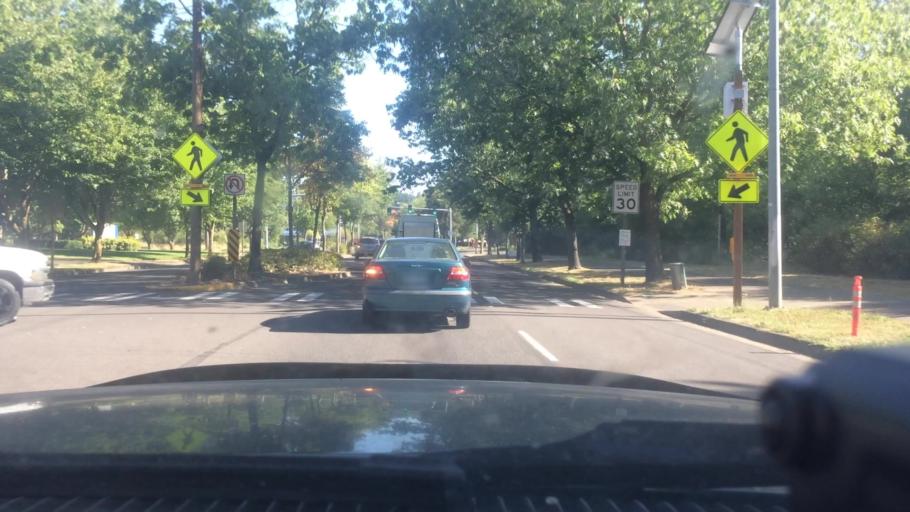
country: US
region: Oregon
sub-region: Lane County
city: Eugene
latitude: 44.0220
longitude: -123.0817
